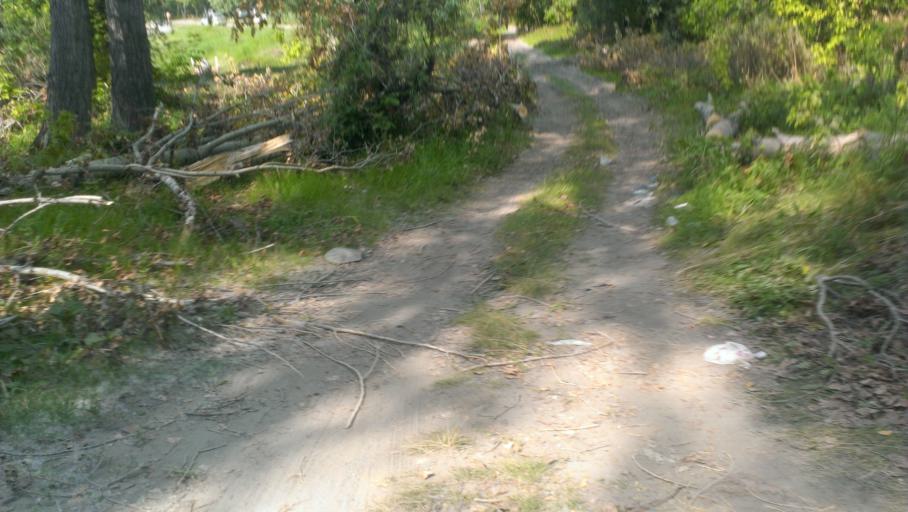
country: RU
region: Altai Krai
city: Novoaltaysk
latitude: 53.3712
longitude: 83.8558
